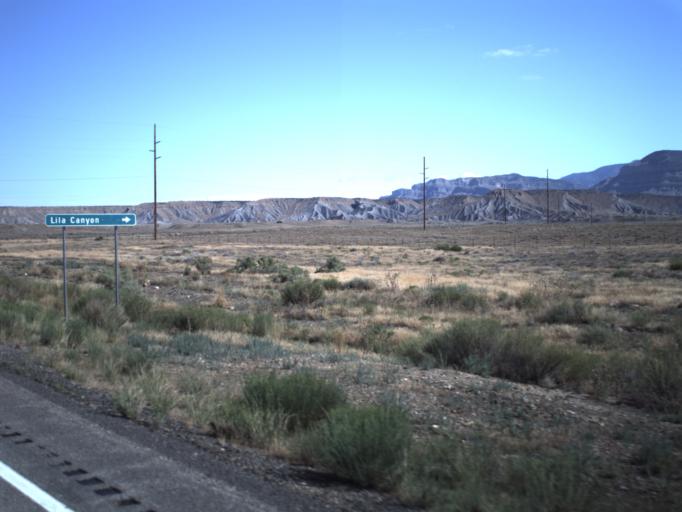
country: US
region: Utah
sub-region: Carbon County
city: East Carbon City
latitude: 39.3681
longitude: -110.3951
